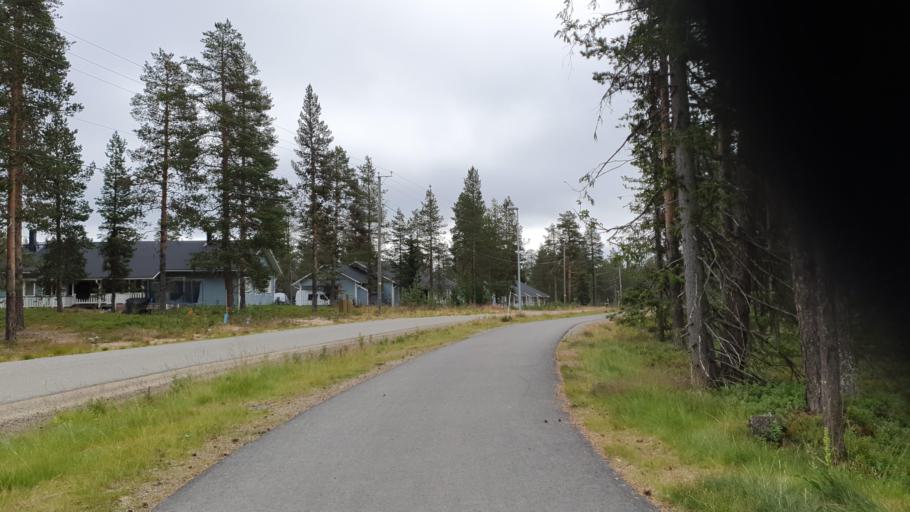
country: FI
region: Lapland
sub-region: Tunturi-Lappi
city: Kolari
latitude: 67.6249
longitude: 24.1459
